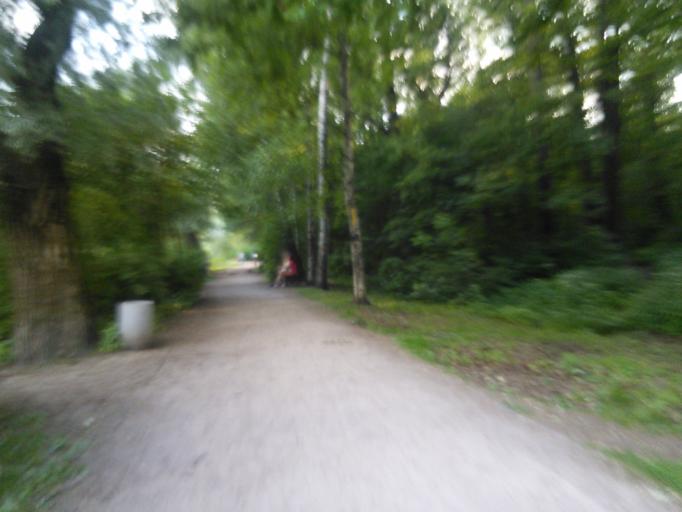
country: RU
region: Moscow
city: Sokol'niki
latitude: 55.8147
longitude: 37.6722
